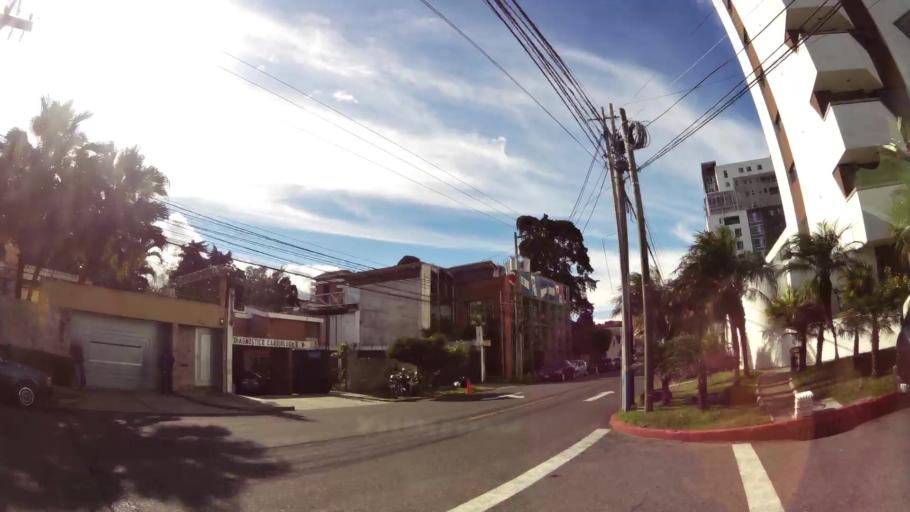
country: GT
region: Guatemala
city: Santa Catarina Pinula
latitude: 14.5845
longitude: -90.5176
